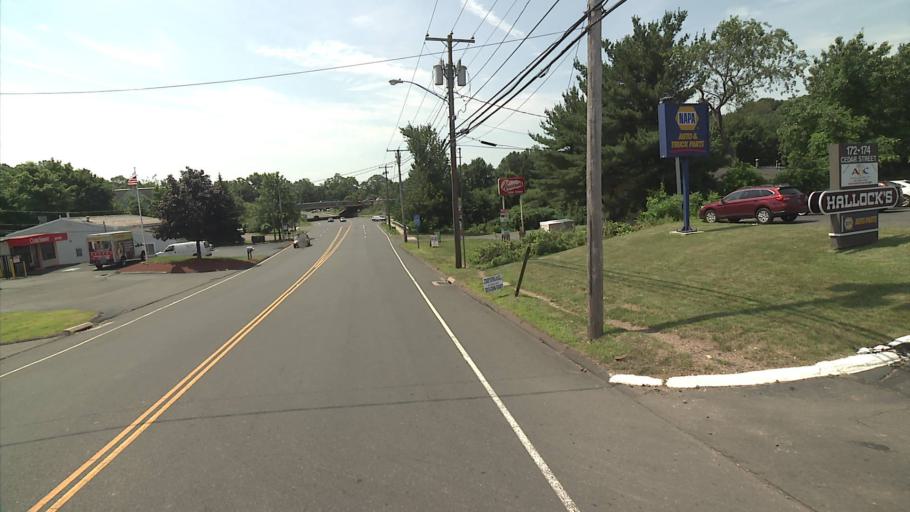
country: US
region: Connecticut
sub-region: New Haven County
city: Branford
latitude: 41.2902
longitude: -72.8194
